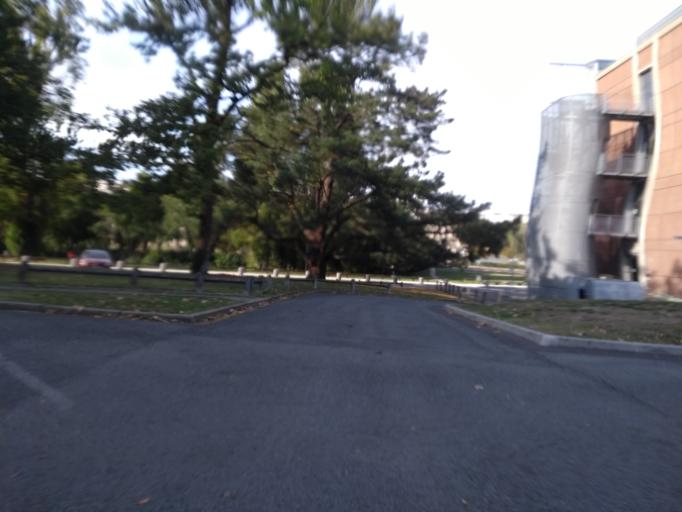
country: FR
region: Aquitaine
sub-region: Departement de la Gironde
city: Talence
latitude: 44.8082
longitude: -0.5925
